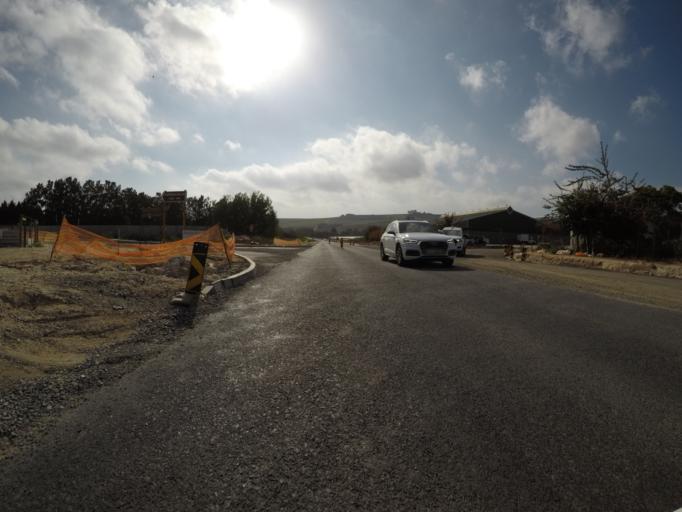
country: ZA
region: Western Cape
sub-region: Cape Winelands District Municipality
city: Stellenbosch
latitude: -33.9856
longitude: 18.7791
